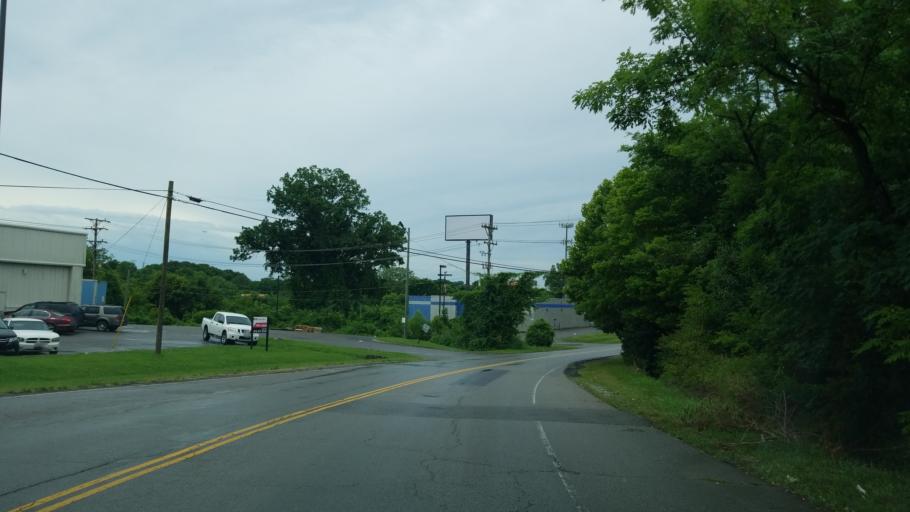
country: US
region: Tennessee
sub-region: Rutherford County
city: La Vergne
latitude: 36.0484
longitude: -86.6599
